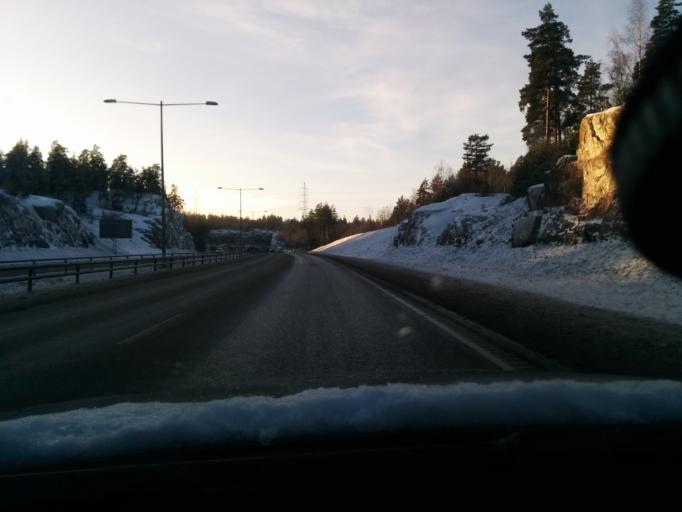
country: SE
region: Stockholm
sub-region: Sollentuna Kommun
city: Sollentuna
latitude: 59.4655
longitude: 17.9738
